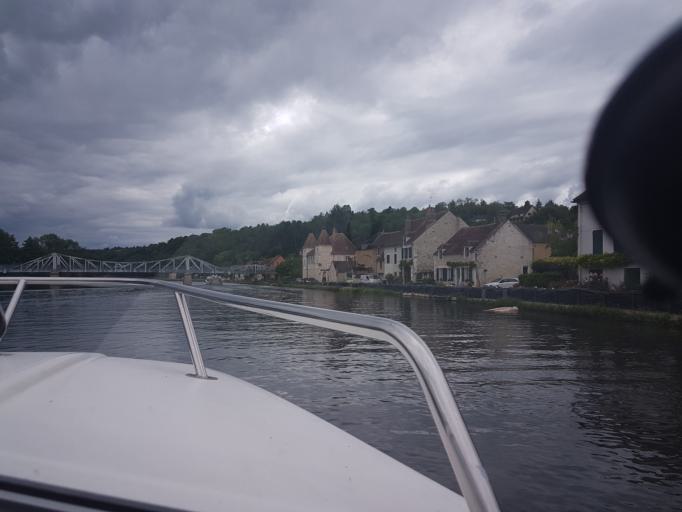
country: FR
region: Bourgogne
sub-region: Departement de l'Yonne
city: Augy
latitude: 47.7558
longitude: 3.5922
